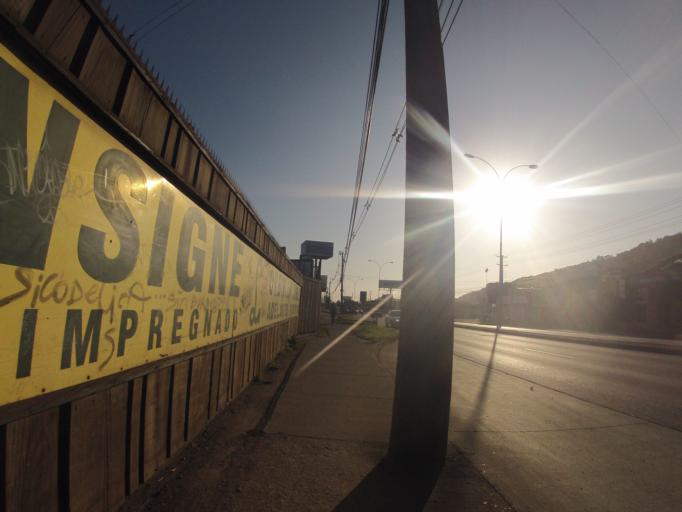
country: CL
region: Araucania
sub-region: Provincia de Cautin
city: Temuco
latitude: -38.7270
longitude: -72.5773
